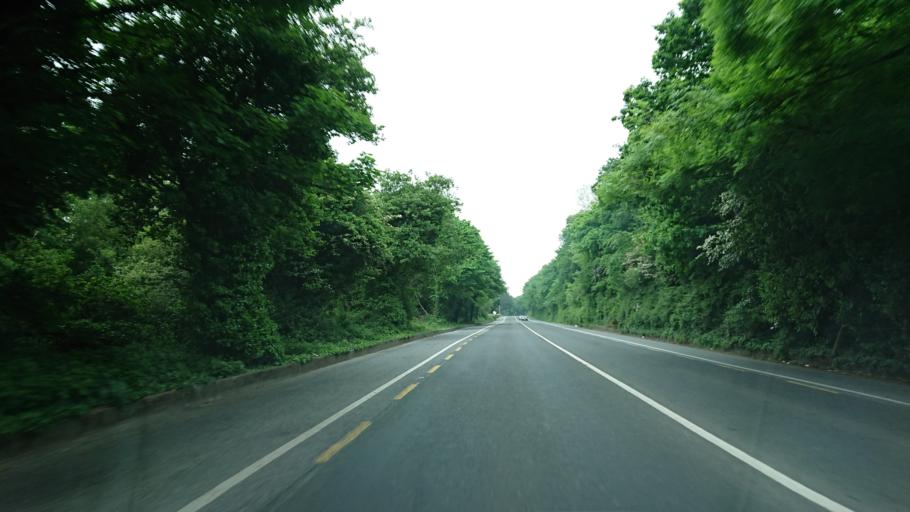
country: IE
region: Munster
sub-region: Waterford
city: Tra Mhor
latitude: 52.1797
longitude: -7.1356
